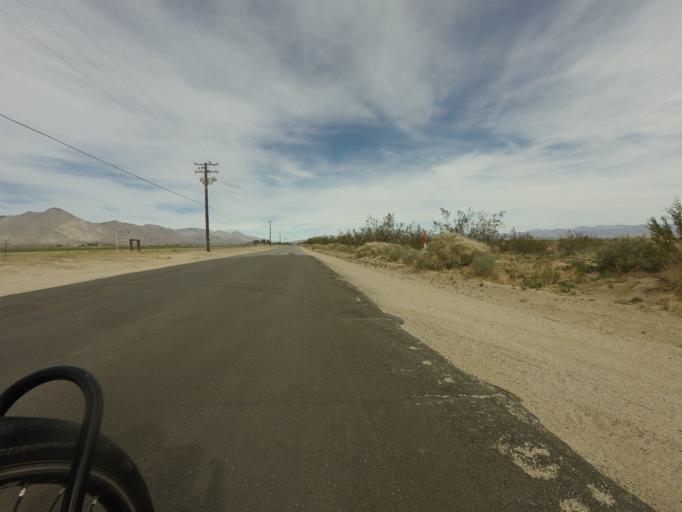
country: US
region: California
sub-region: Kern County
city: Inyokern
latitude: 35.7398
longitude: -117.8399
